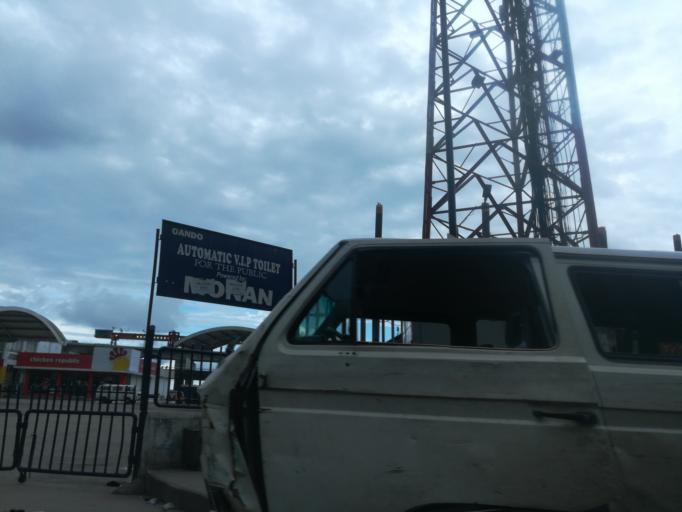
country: NG
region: Lagos
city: Lagos
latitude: 6.4536
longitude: 3.3854
